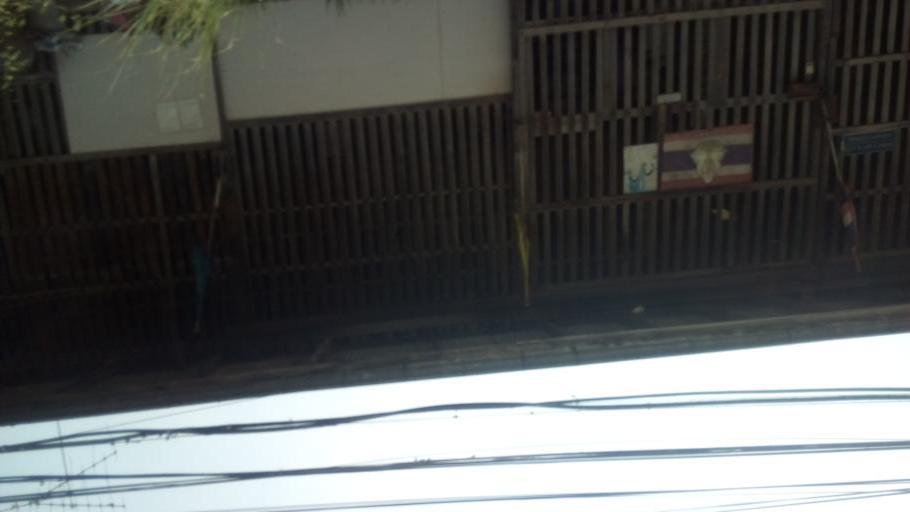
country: TH
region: Nakhon Pathom
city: Salaya
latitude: 13.7567
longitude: 100.2826
